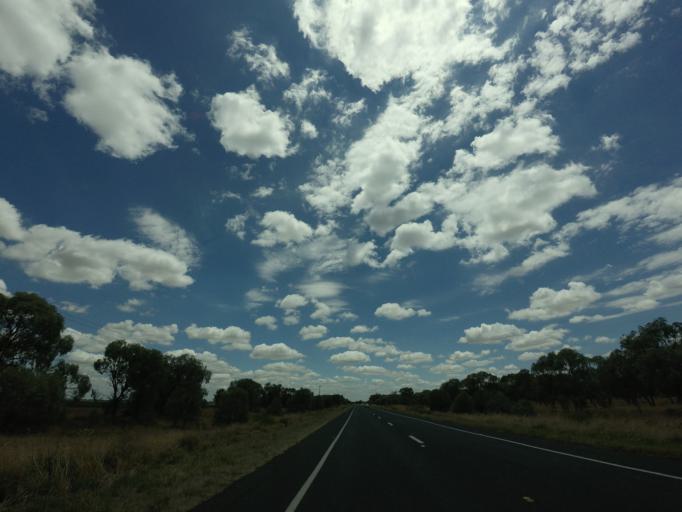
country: AU
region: New South Wales
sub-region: Moree Plains
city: Boggabilla
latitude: -28.9067
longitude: 150.1347
